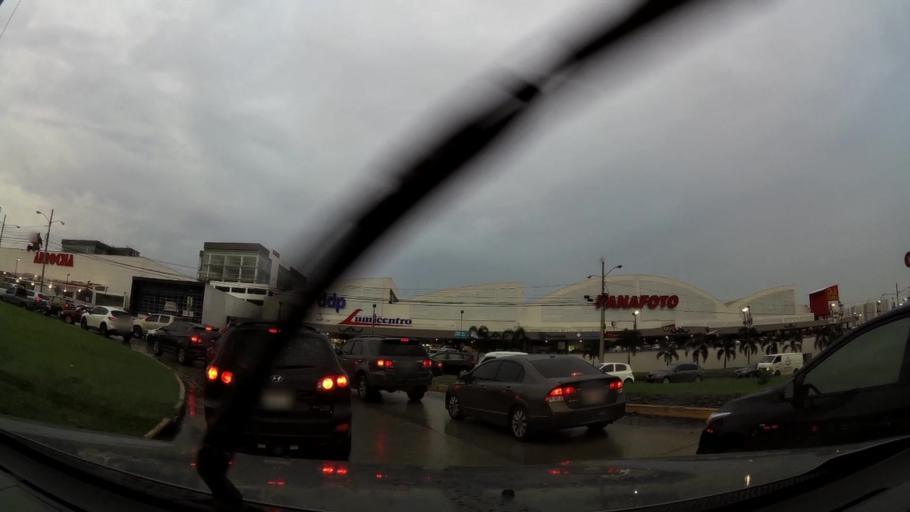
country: PA
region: Panama
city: Panama
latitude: 9.0304
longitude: -79.5330
